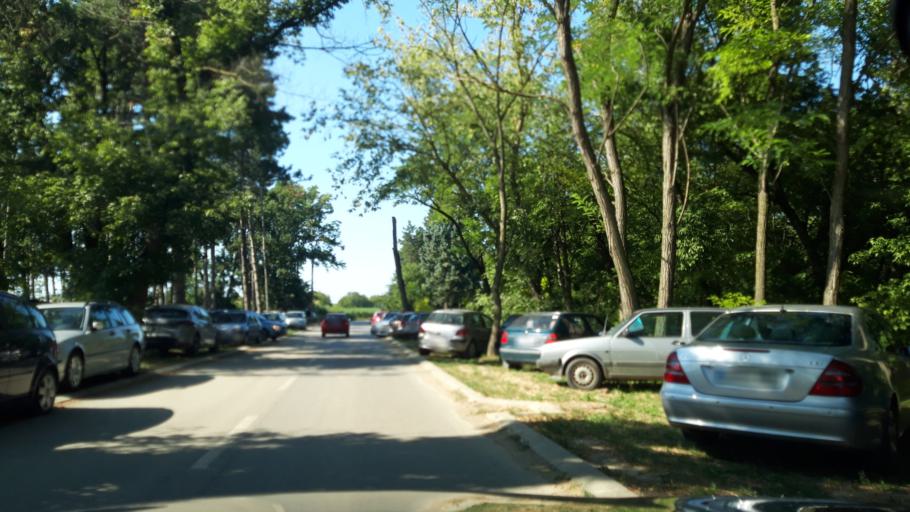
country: RS
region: Autonomna Pokrajina Vojvodina
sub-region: Sremski Okrug
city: Ruma
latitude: 45.0351
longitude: 19.8188
